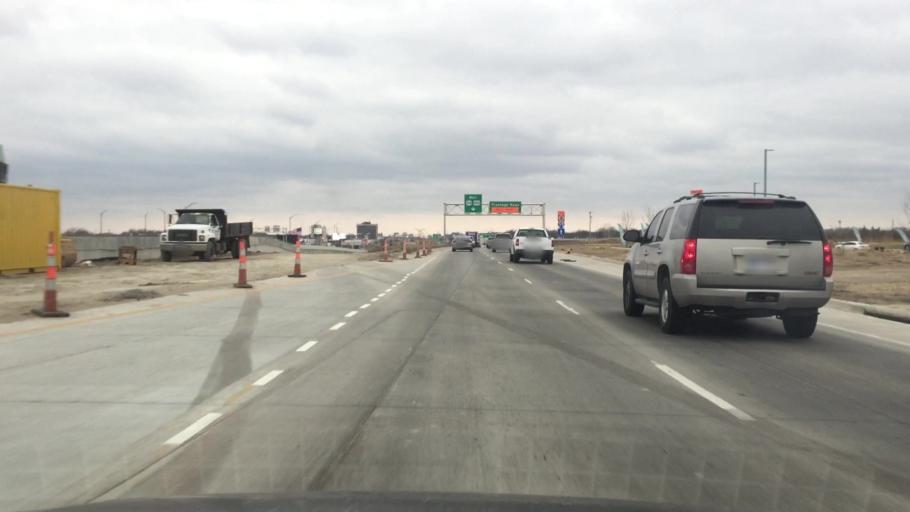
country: US
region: Kansas
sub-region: Sedgwick County
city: Bellaire
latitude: 37.6795
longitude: -97.2271
